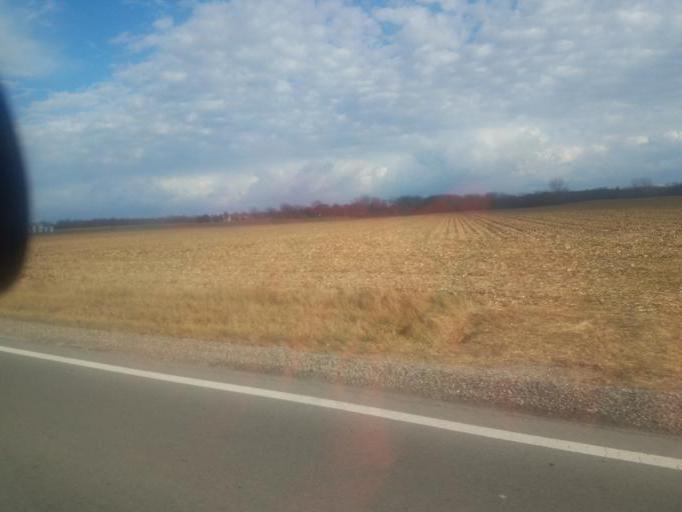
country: US
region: Ohio
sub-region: Marion County
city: Prospect
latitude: 40.4801
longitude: -83.0700
